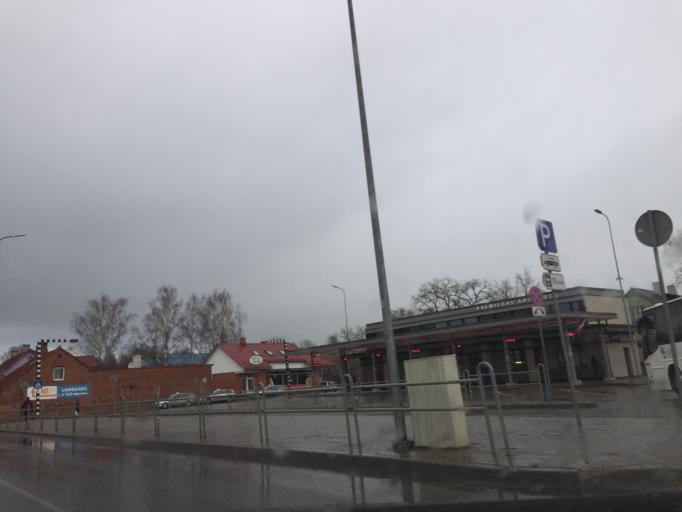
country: LV
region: Valmieras Rajons
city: Valmiera
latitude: 57.5341
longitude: 25.4258
